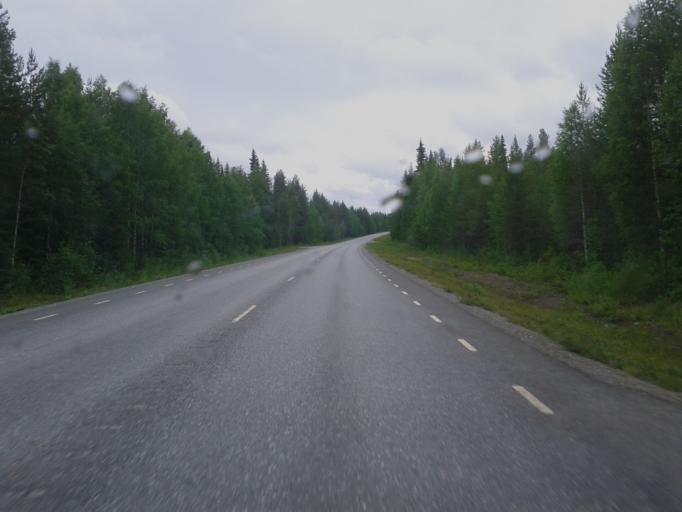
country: SE
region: Vaesterbotten
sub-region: Skelleftea Kommun
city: Langsele
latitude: 64.8957
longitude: 20.1567
